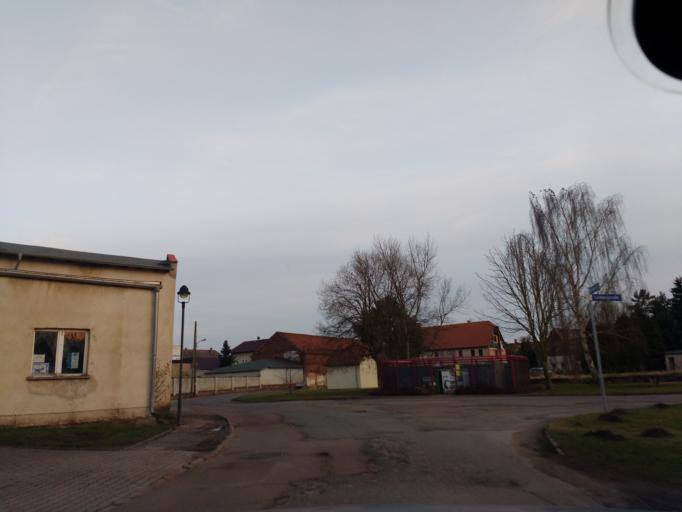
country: DE
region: Saxony-Anhalt
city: Halle (Saale)
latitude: 51.5187
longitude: 12.0110
